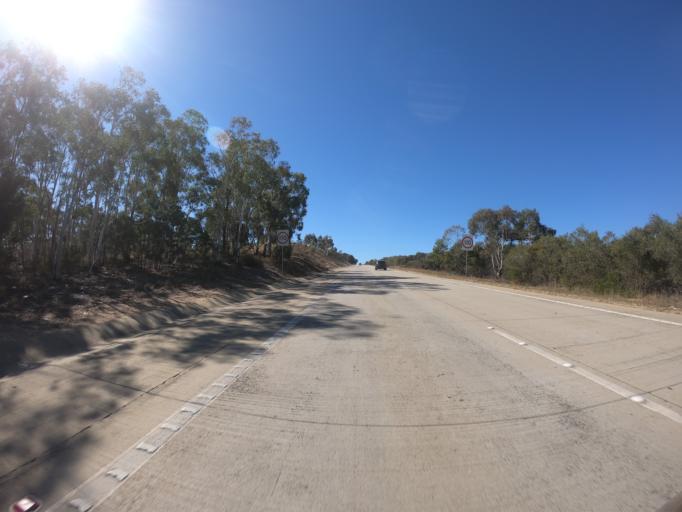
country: AU
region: New South Wales
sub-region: Yass Valley
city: Gundaroo
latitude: -35.1161
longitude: 149.3542
